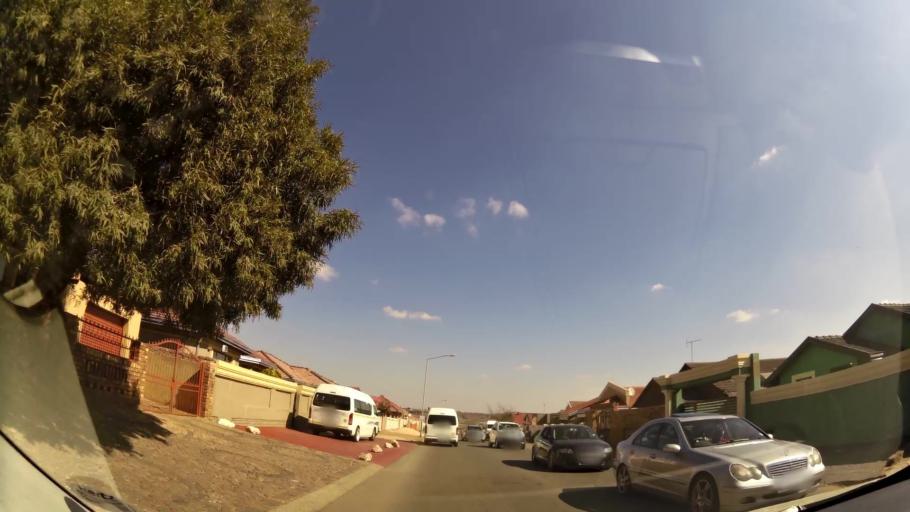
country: ZA
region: Gauteng
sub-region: West Rand District Municipality
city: Krugersdorp
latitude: -26.1537
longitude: 27.7716
